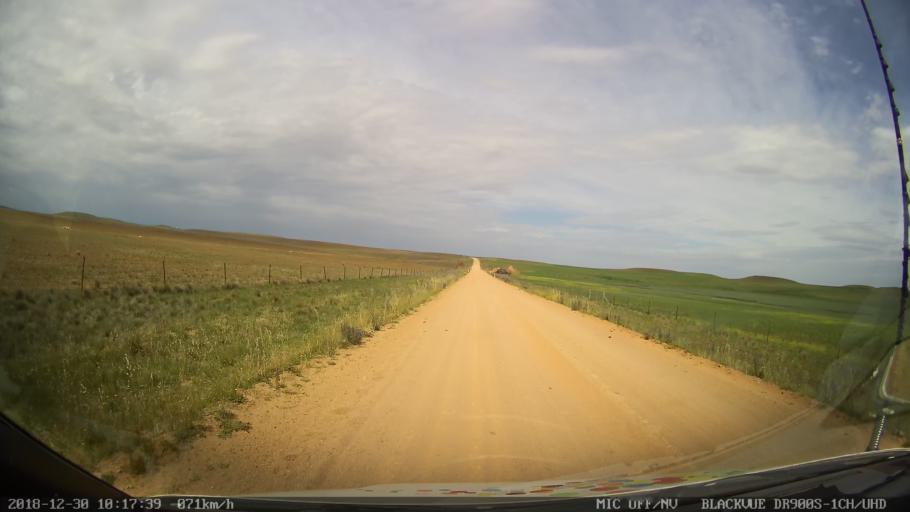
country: AU
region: New South Wales
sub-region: Snowy River
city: Berridale
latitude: -36.5492
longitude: 149.0185
